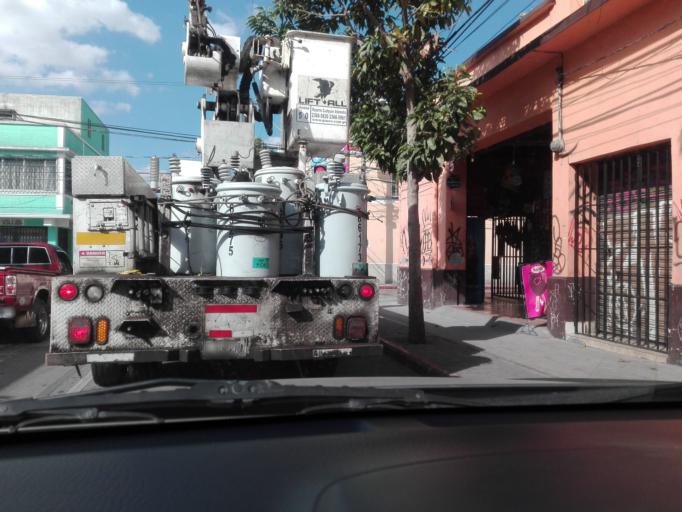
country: GT
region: Guatemala
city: Guatemala City
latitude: 14.6446
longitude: -90.5145
